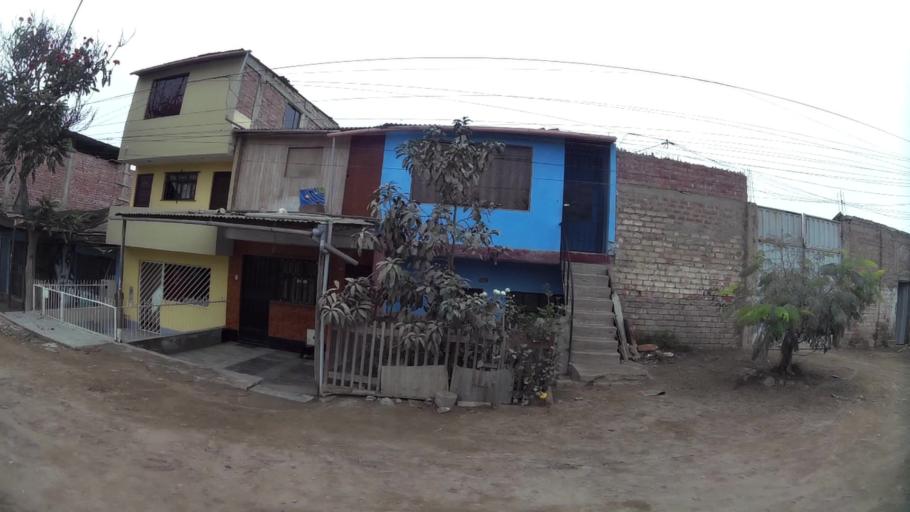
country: PE
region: Lima
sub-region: Lima
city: Surco
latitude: -12.1847
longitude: -76.9270
